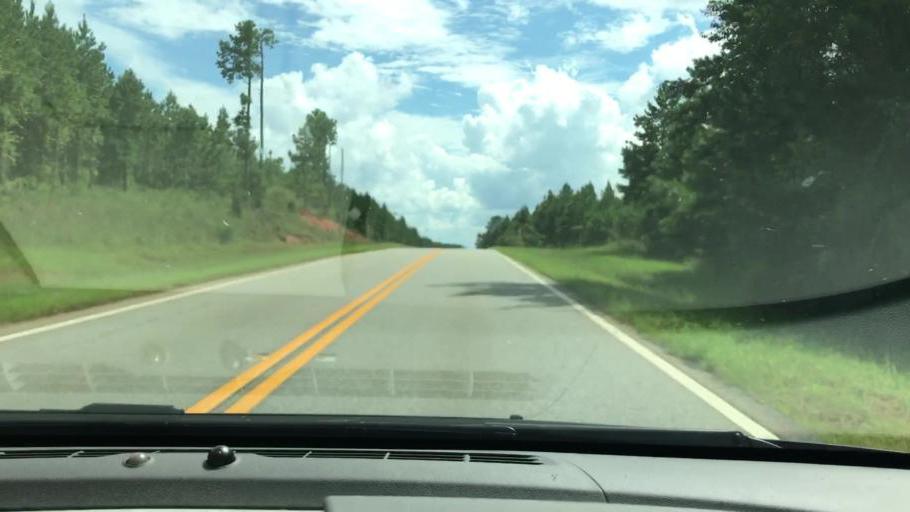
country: US
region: Georgia
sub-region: Quitman County
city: Georgetown
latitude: 31.9211
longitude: -85.0598
